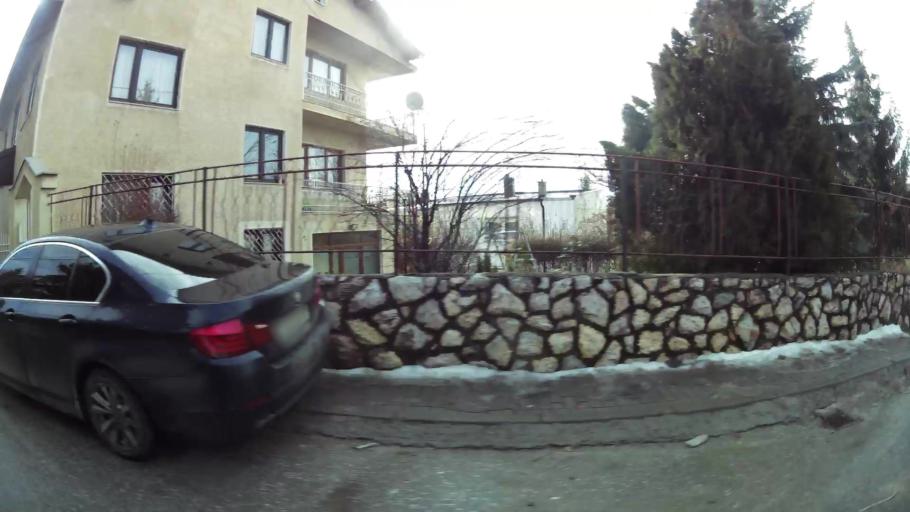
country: XK
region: Pristina
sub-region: Komuna e Prishtines
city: Pristina
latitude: 42.6690
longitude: 21.1743
